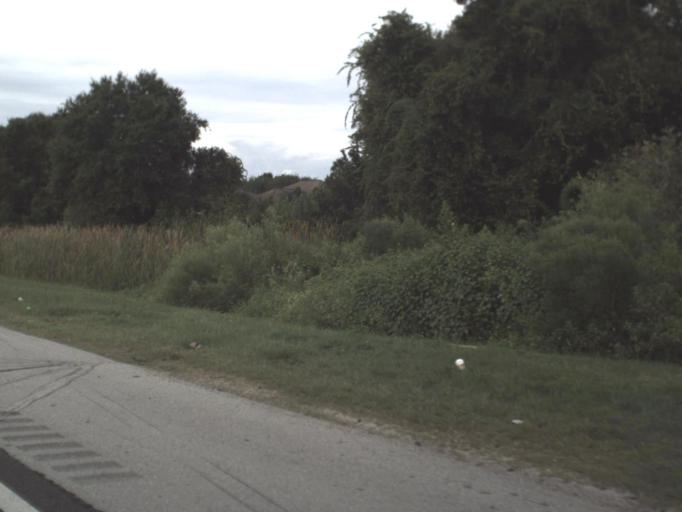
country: US
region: Florida
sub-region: Sarasota County
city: Lake Sarasota
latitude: 27.2837
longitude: -82.4490
